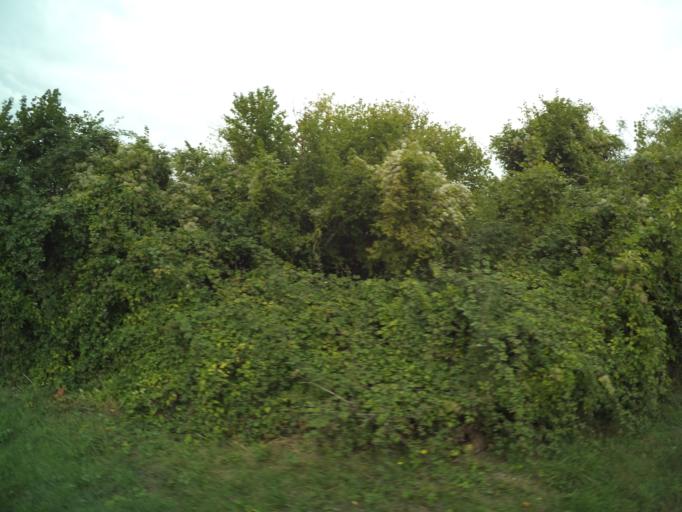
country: FR
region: Centre
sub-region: Departement d'Indre-et-Loire
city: Auzouer-en-Touraine
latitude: 47.5118
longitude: 0.9316
